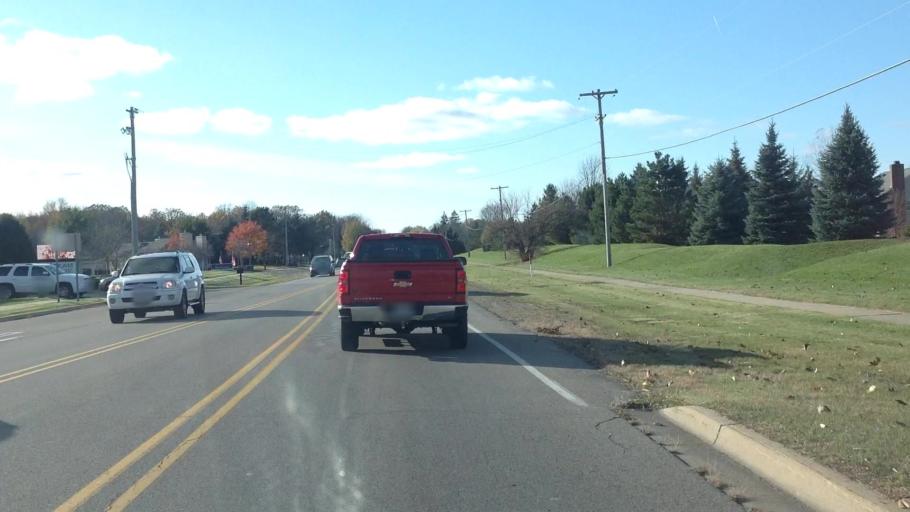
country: US
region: Michigan
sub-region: Saginaw County
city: Saginaw
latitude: 43.4654
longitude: -83.9960
